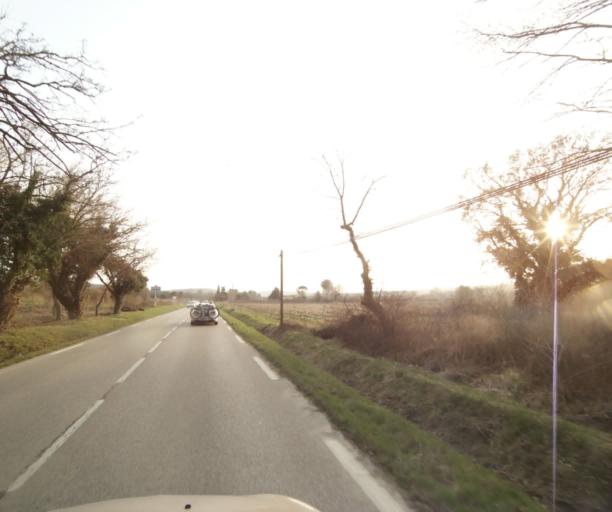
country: FR
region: Provence-Alpes-Cote d'Azur
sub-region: Departement des Bouches-du-Rhone
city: Rognes
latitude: 43.7011
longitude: 5.3480
